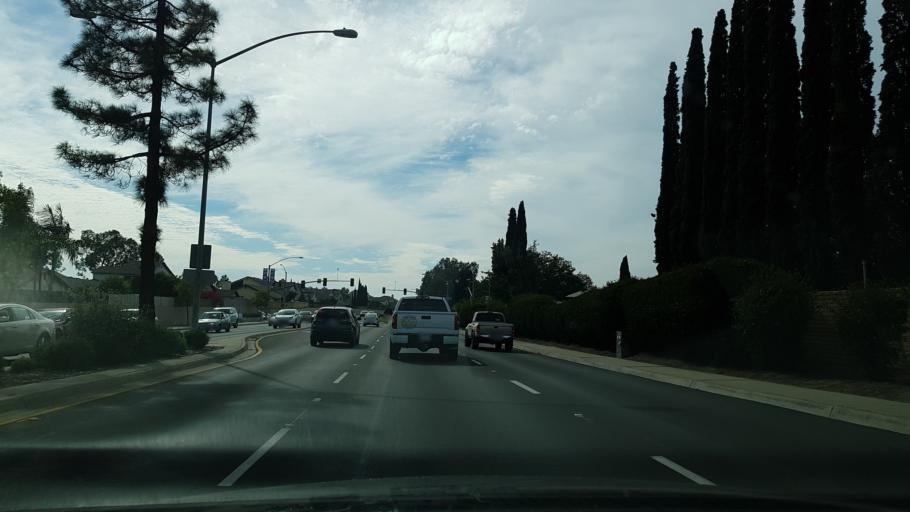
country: US
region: California
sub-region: San Diego County
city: Fairbanks Ranch
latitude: 32.9114
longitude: -117.1542
